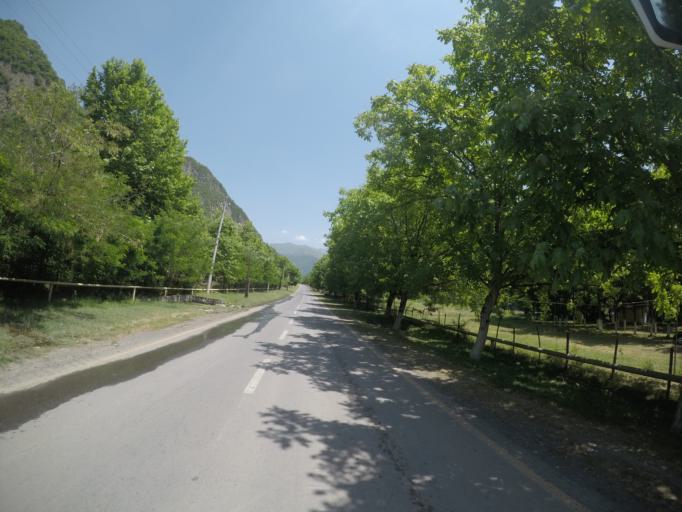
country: AZ
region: Qakh Rayon
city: Qaxbas
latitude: 41.4520
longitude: 47.0091
